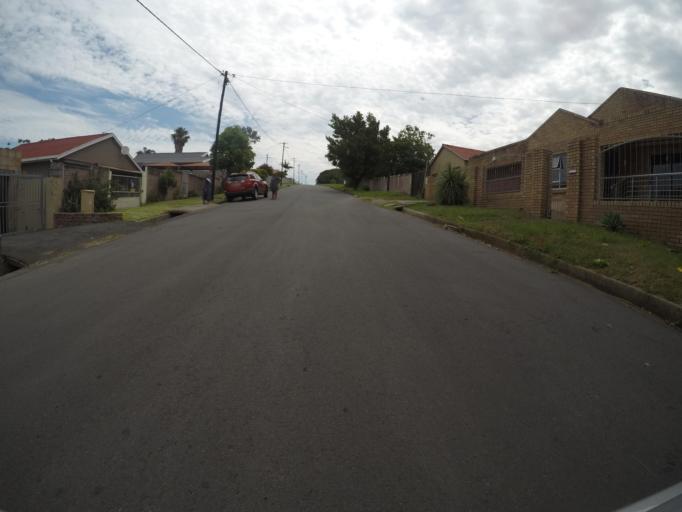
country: ZA
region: Eastern Cape
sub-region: Buffalo City Metropolitan Municipality
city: East London
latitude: -32.9945
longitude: 27.8807
